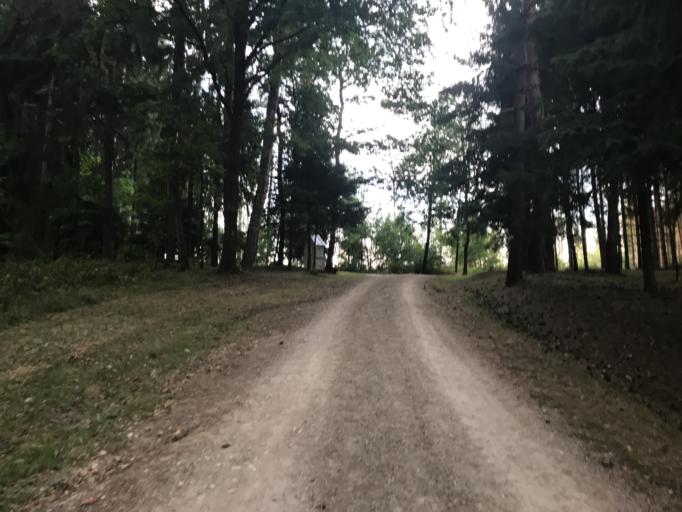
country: DE
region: Bavaria
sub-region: Upper Palatinate
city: Auerbach
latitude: 49.7155
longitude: 11.6336
